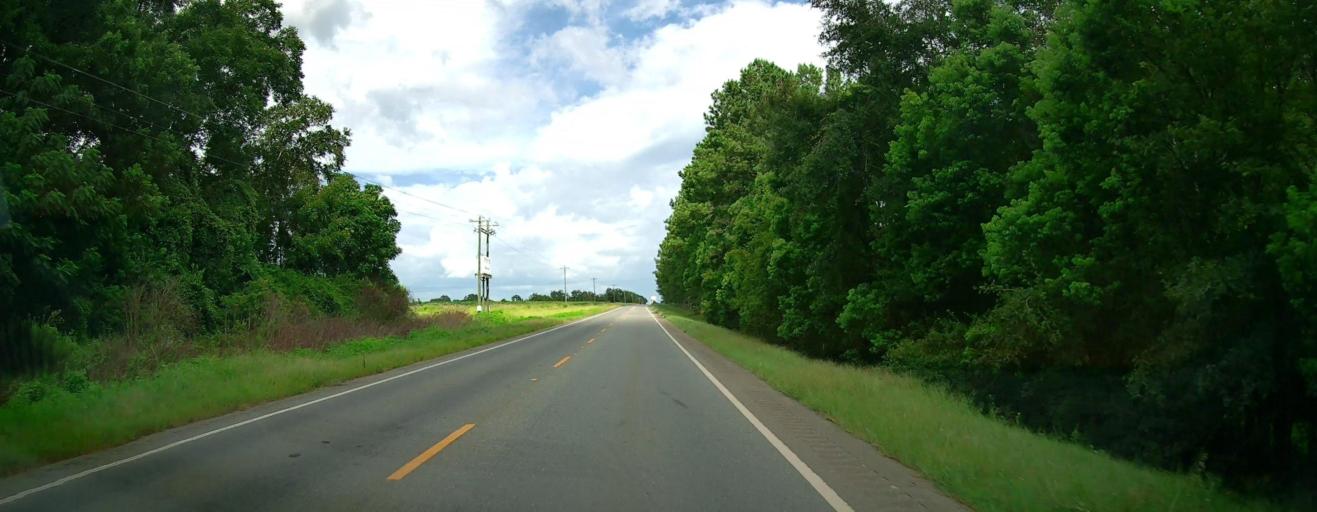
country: US
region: Georgia
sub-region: Coffee County
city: Douglas
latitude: 31.5390
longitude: -82.8785
